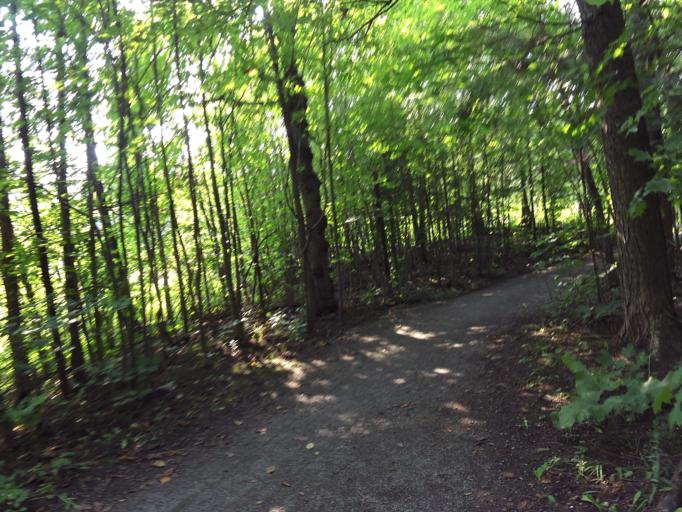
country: CA
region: Ontario
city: Bells Corners
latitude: 45.3377
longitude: -75.9244
